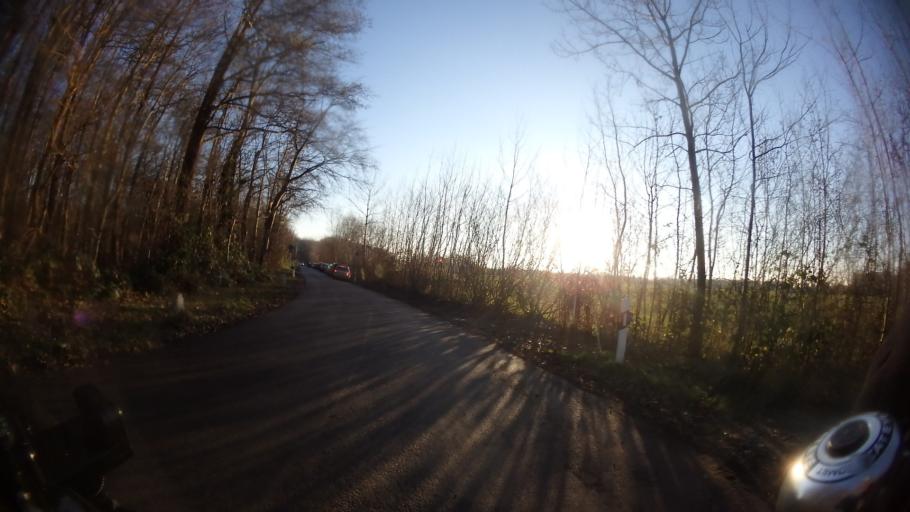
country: DE
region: Schleswig-Holstein
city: Travemuende
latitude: 53.9869
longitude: 10.8719
